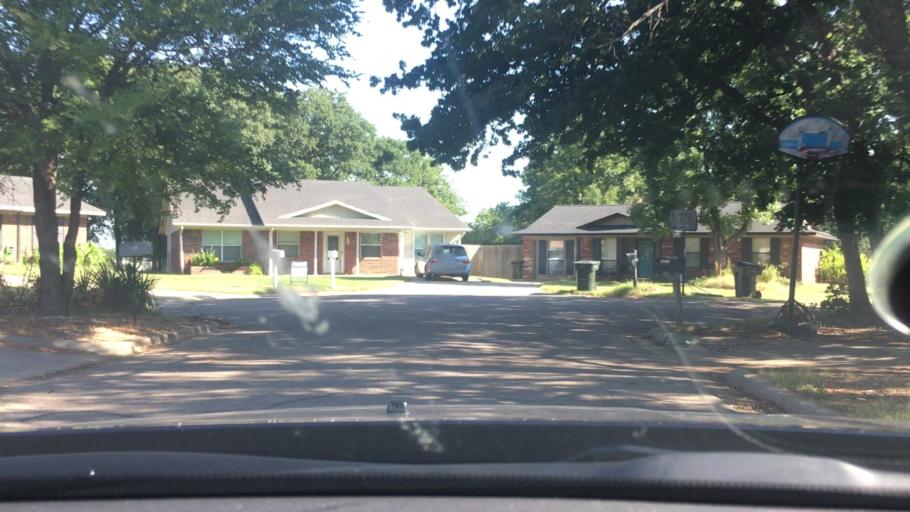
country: US
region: Oklahoma
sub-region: Bryan County
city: Durant
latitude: 34.0133
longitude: -96.3877
